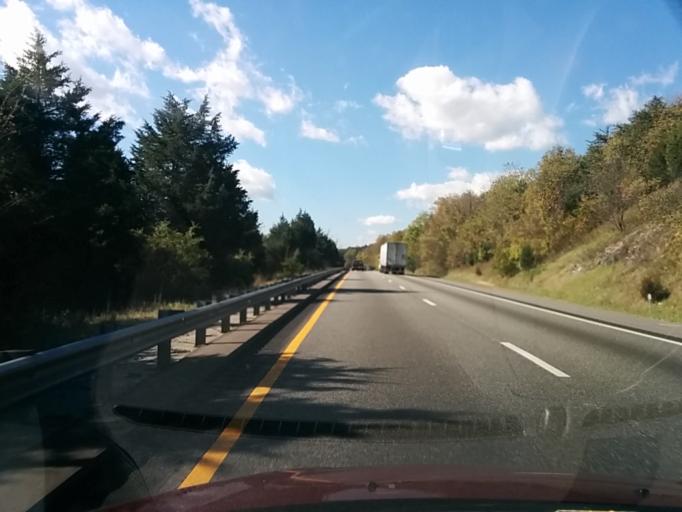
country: US
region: Virginia
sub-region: Botetourt County
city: Fincastle
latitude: 37.4716
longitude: -79.8053
